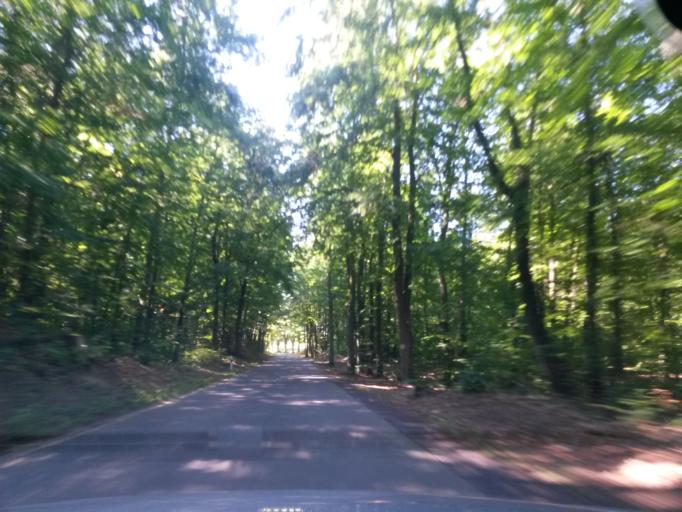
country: DE
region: Brandenburg
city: Lychen
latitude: 53.1426
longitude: 13.3761
